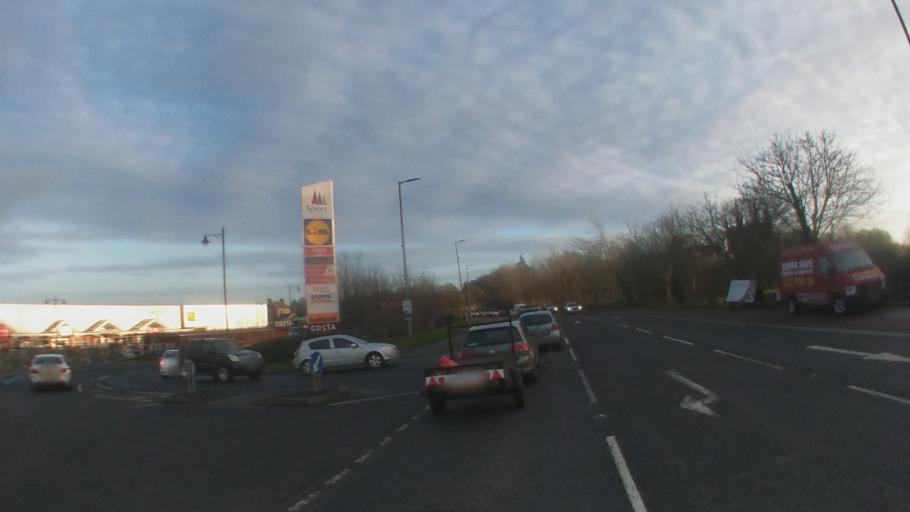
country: GB
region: Northern Ireland
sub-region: Armagh District
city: Armagh
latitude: 54.3564
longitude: -6.6622
